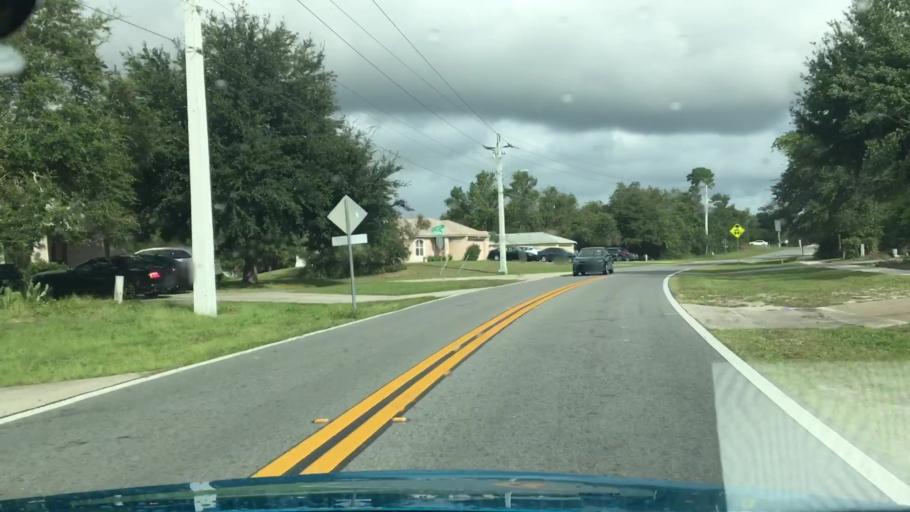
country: US
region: Florida
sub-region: Volusia County
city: Lake Helen
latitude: 28.9514
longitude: -81.1865
